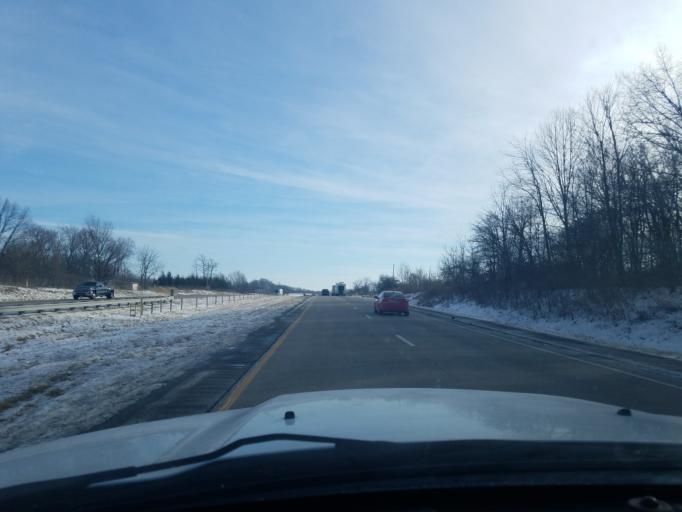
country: US
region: Indiana
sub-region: Grant County
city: Upland
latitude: 40.4542
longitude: -85.5495
